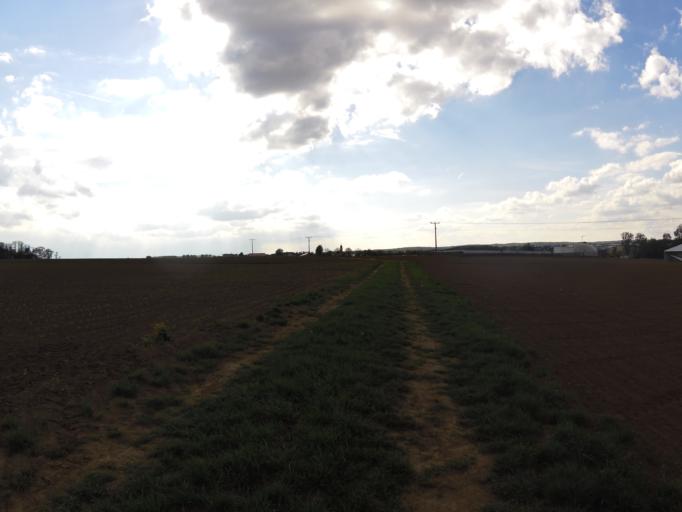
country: DE
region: Bavaria
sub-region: Regierungsbezirk Unterfranken
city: Unterpleichfeld
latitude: 49.8663
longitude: 10.0623
